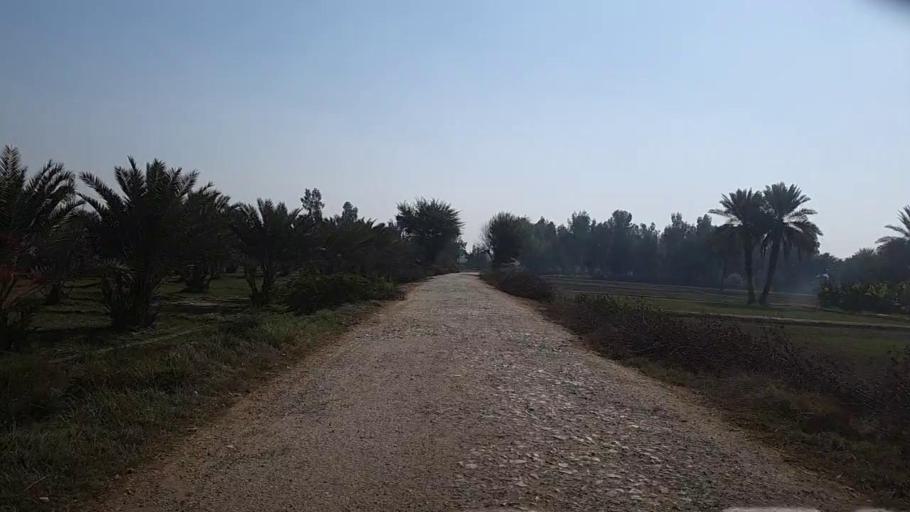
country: PK
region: Sindh
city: Bozdar
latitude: 27.1947
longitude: 68.6383
